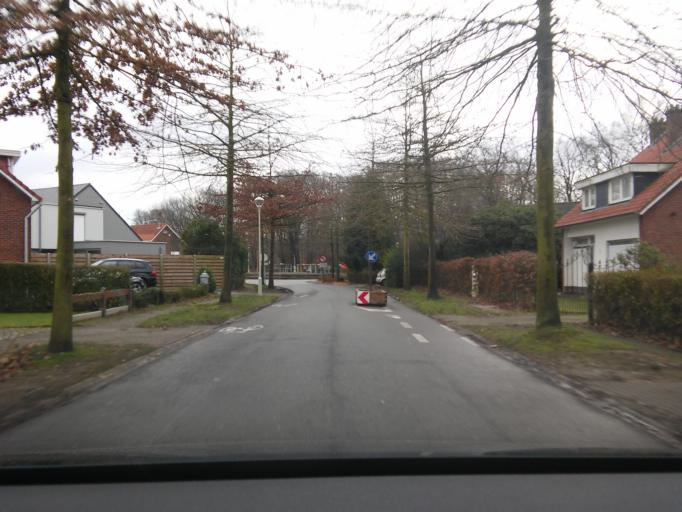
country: BE
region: Flanders
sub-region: Provincie Antwerpen
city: Rumst
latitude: 51.0840
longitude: 4.4397
